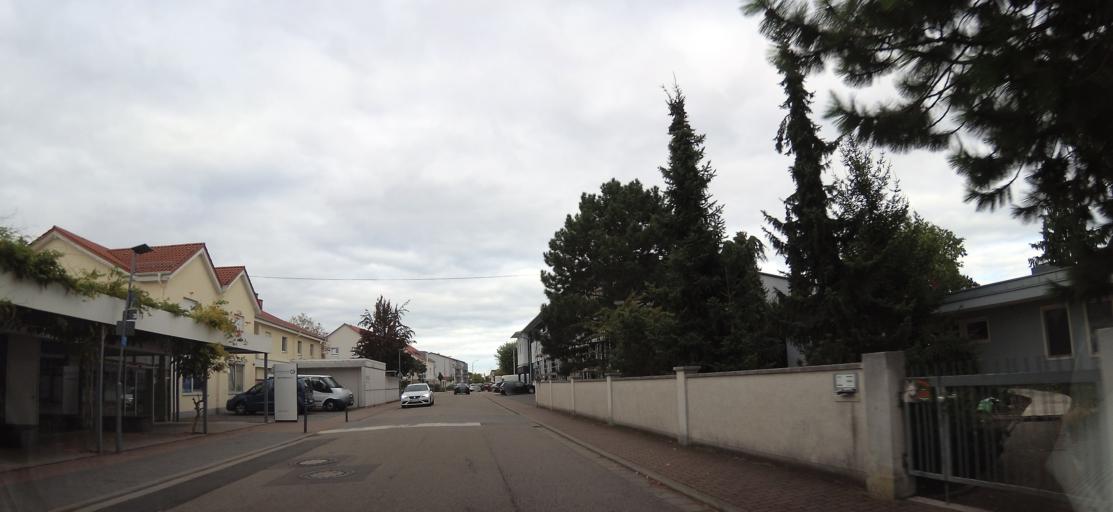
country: DE
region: Rheinland-Pfalz
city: Offenbach an der Queich
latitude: 49.1985
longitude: 8.1950
